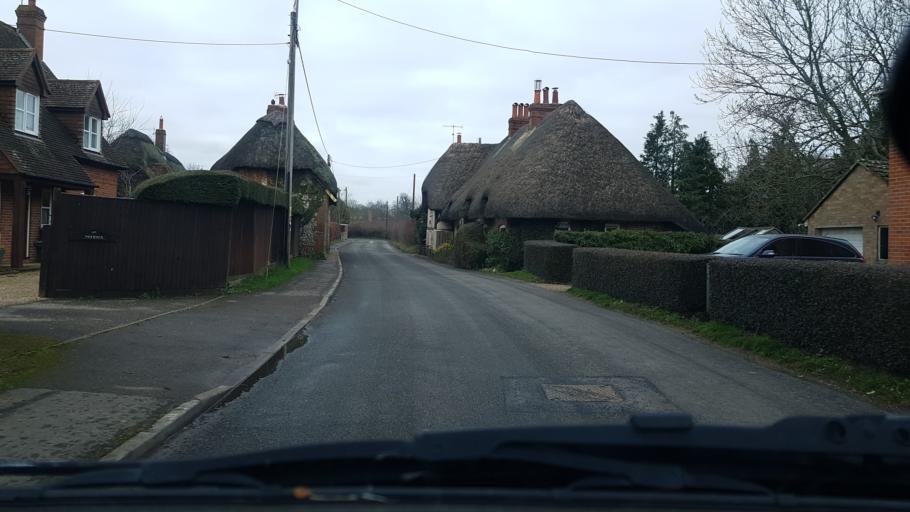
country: GB
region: England
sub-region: Hampshire
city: Andover
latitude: 51.2794
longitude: -1.4547
